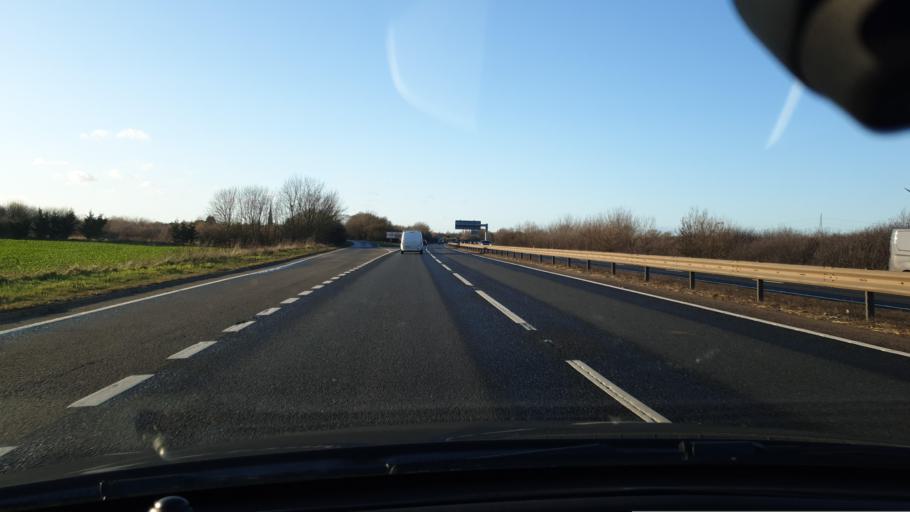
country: GB
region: England
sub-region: Cambridgeshire
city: Buckden
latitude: 52.3320
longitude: -0.2839
